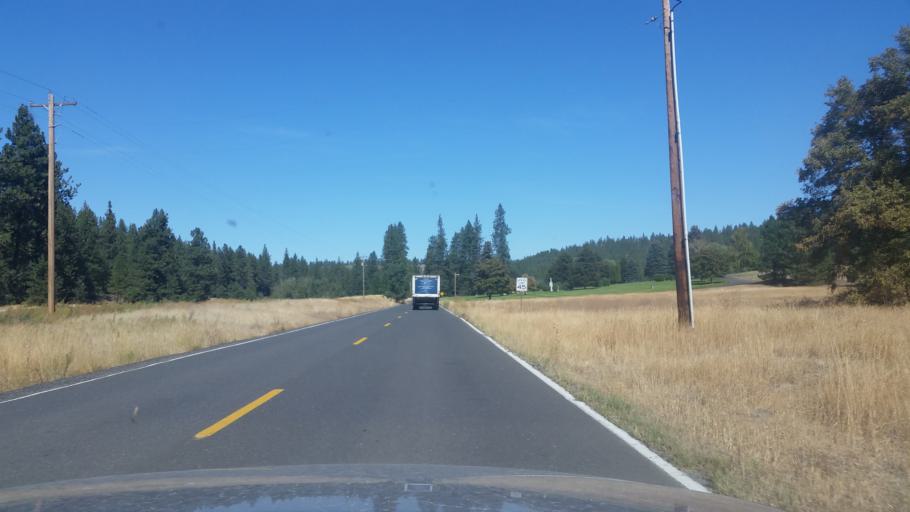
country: US
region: Washington
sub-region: Spokane County
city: Spokane
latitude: 47.5953
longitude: -117.4463
